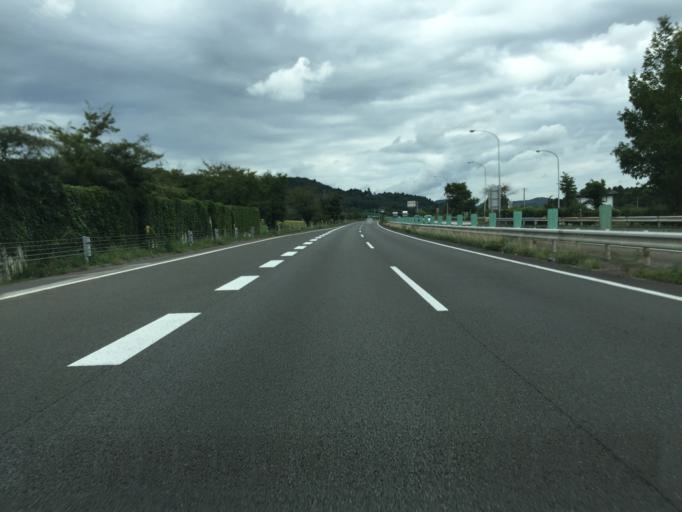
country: JP
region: Miyagi
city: Shiroishi
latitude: 38.0396
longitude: 140.6326
